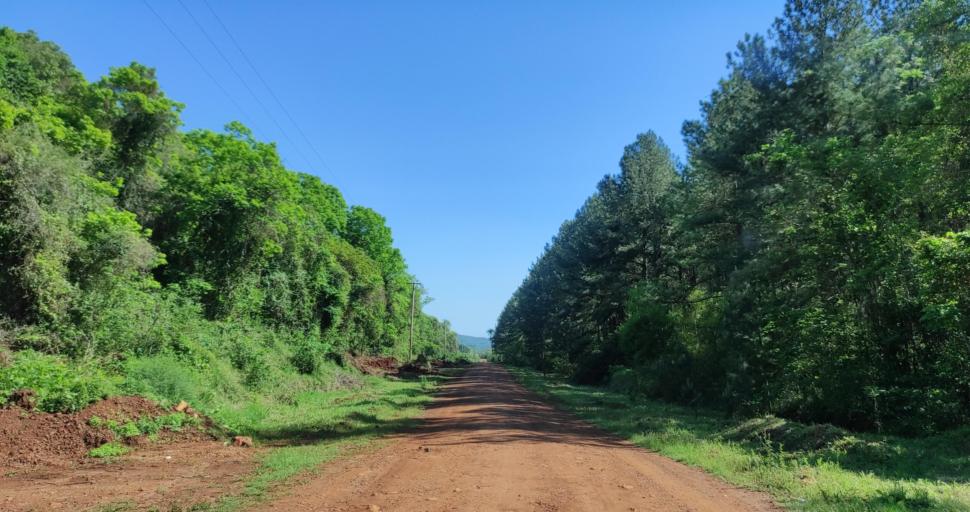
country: AR
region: Misiones
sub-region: Departamento de Candelaria
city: Loreto
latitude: -27.3293
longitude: -55.5245
